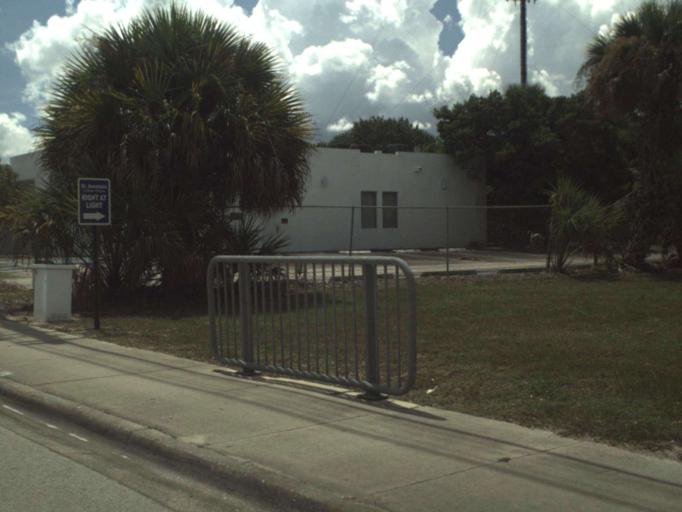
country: US
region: Florida
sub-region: Saint Lucie County
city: Fort Pierce North
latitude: 27.4474
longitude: -80.3609
